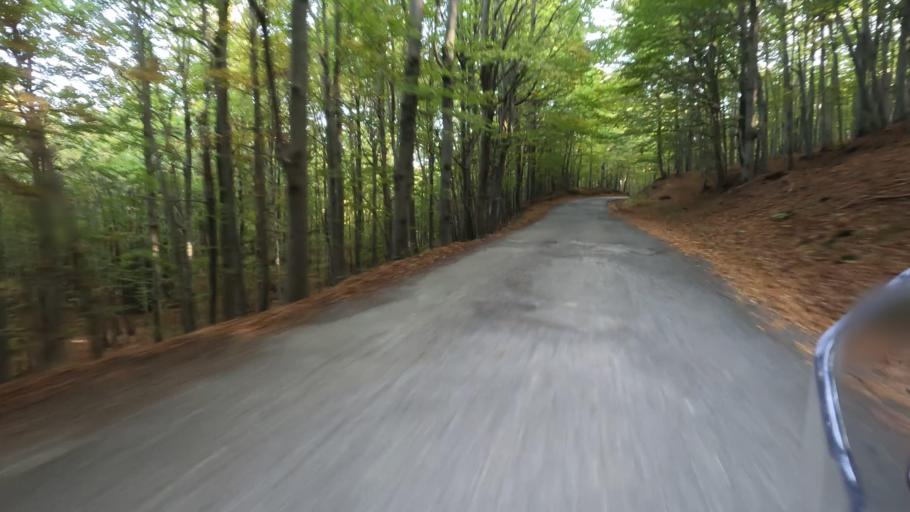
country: IT
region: Liguria
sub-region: Provincia di Savona
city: Urbe
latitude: 44.4422
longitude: 8.5797
